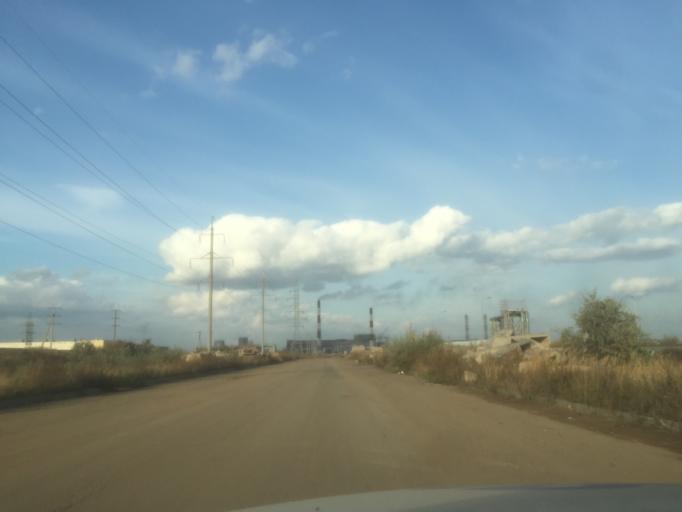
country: KZ
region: Astana Qalasy
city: Astana
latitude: 51.1735
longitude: 71.4953
